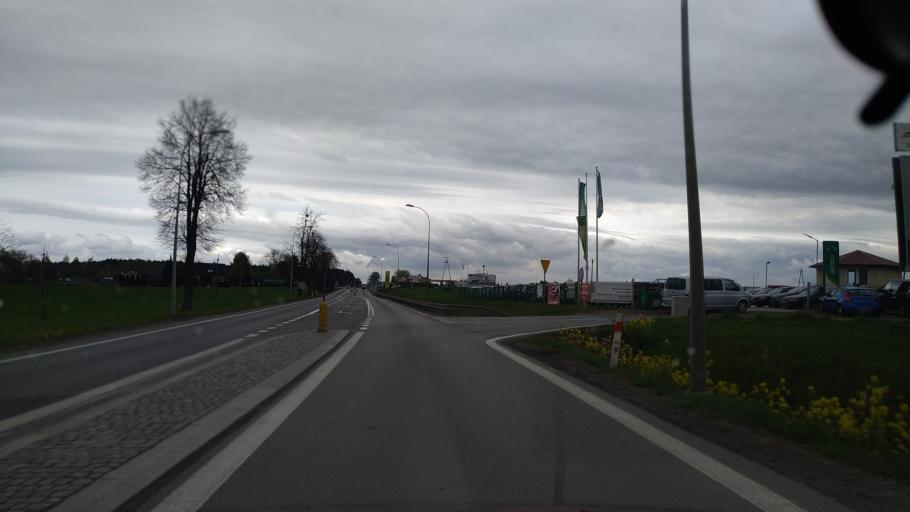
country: PL
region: Pomeranian Voivodeship
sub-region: Powiat starogardzki
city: Starogard Gdanski
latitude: 53.9523
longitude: 18.4821
